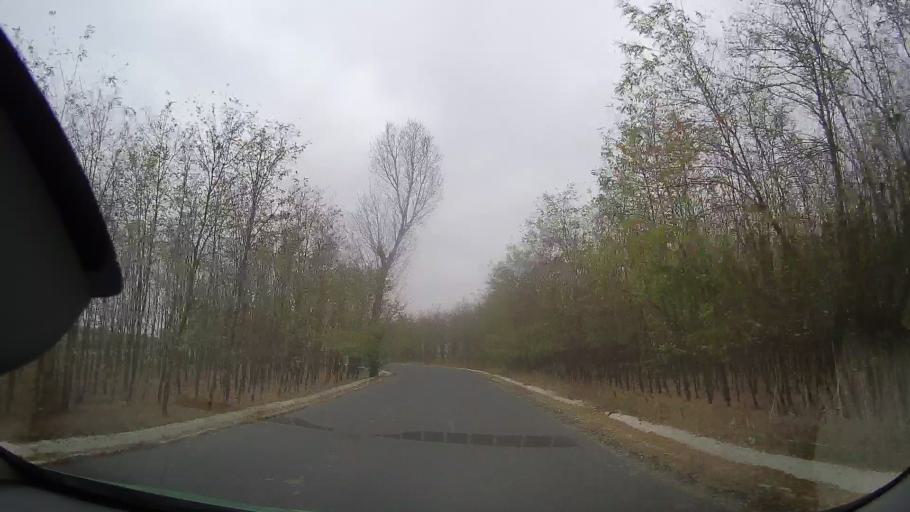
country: RO
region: Braila
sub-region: Comuna Ciocile
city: Ciocile
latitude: 44.7969
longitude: 27.2753
